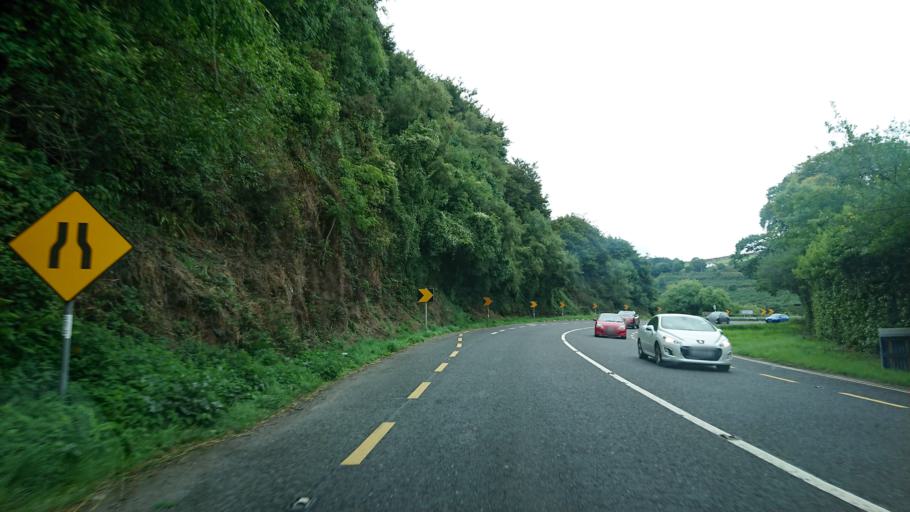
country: IE
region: Munster
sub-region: County Cork
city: Youghal
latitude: 51.9795
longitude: -7.8592
